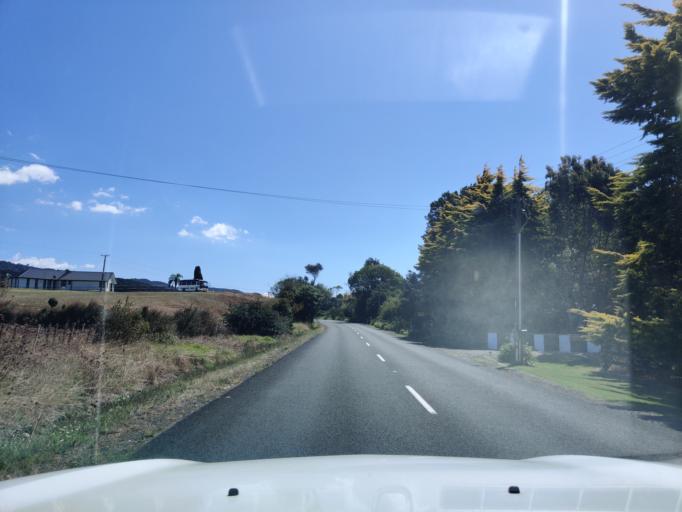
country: NZ
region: Waikato
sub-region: Thames-Coromandel District
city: Thames
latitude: -37.0455
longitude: 175.2981
